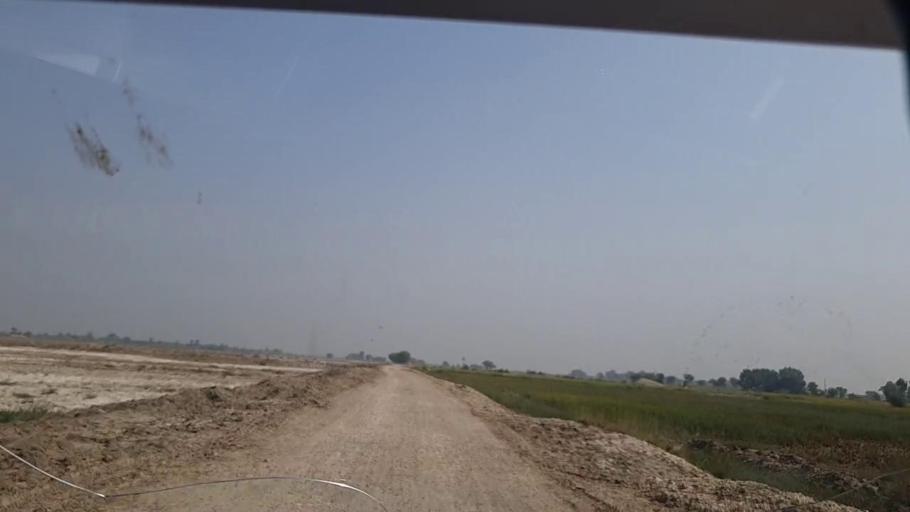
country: PK
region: Sindh
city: Shikarpur
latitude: 28.0513
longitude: 68.6622
